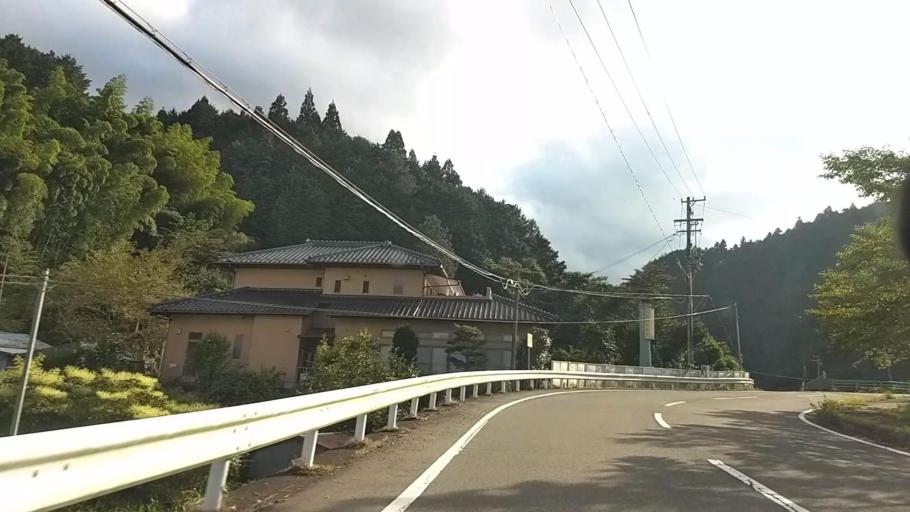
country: JP
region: Shizuoka
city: Fujinomiya
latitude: 35.1780
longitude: 138.5423
